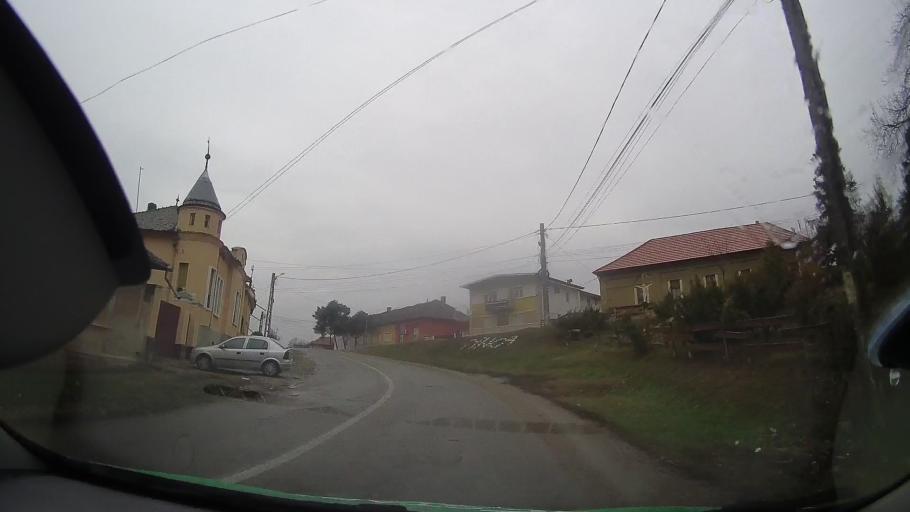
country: RO
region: Bihor
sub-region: Comuna Tinca
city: Tinca
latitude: 46.7733
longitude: 21.9291
